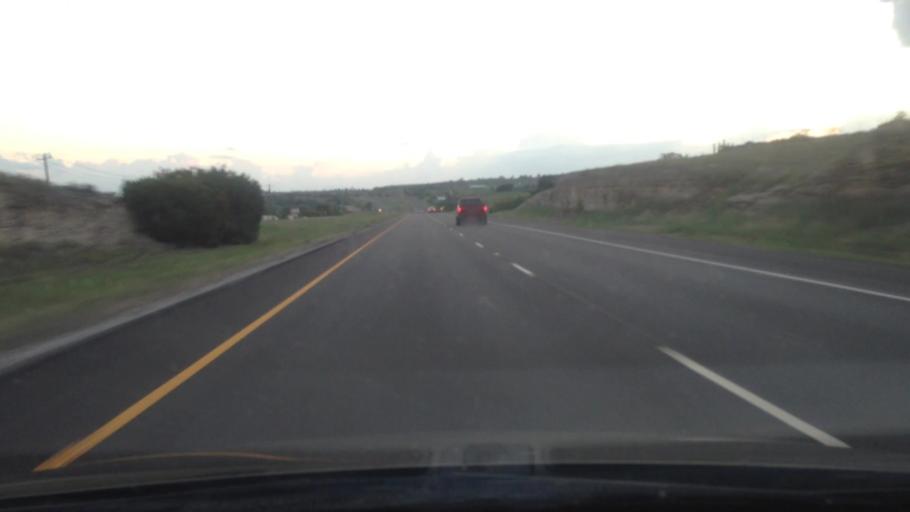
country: US
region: Texas
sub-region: Hood County
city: DeCordova
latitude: 32.5113
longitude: -97.6357
